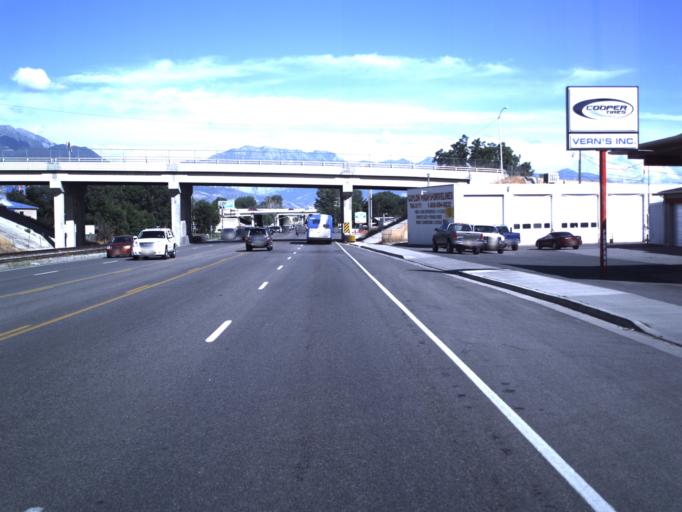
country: US
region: Utah
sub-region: Utah County
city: Lehi
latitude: 40.3947
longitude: -111.8420
